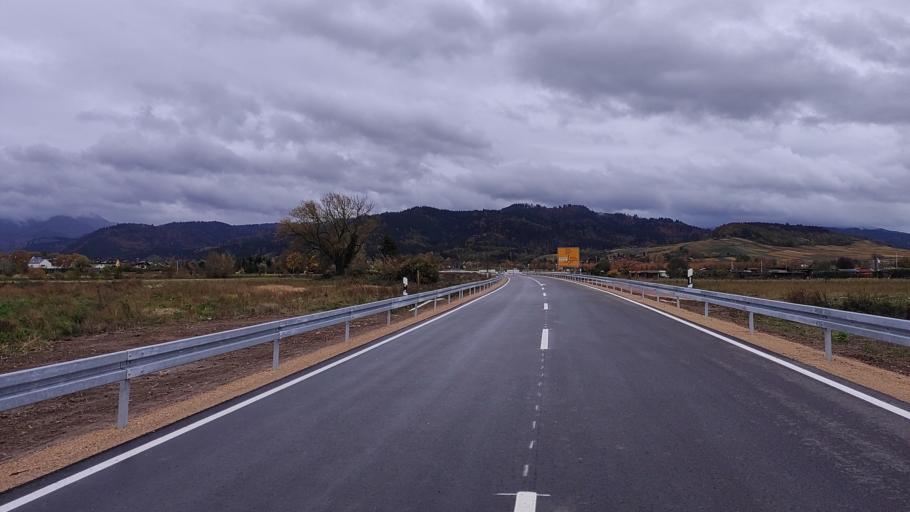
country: DE
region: Baden-Wuerttemberg
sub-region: Freiburg Region
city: Bad Krozingen
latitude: 47.8842
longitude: 7.7144
